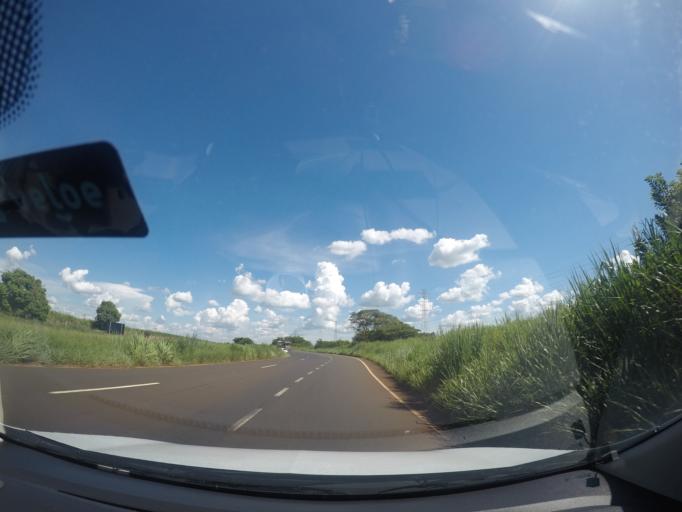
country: BR
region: Sao Paulo
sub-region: Barretos
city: Barretos
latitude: -20.3021
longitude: -48.6663
